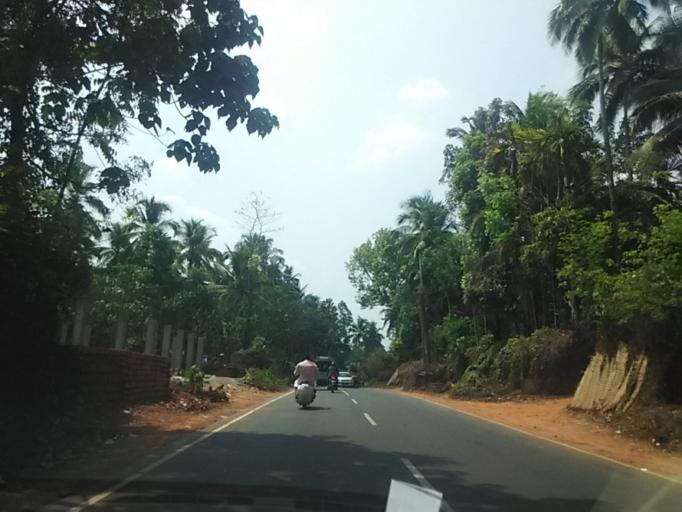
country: IN
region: Kerala
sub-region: Kozhikode
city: Naduvannur
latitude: 11.4927
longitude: 75.7746
